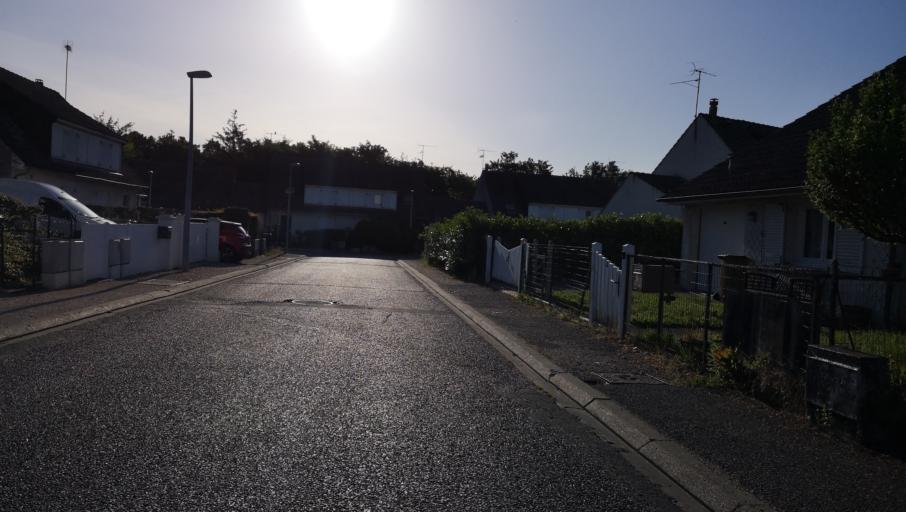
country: FR
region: Centre
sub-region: Departement du Loiret
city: Semoy
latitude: 47.9125
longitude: 1.9344
